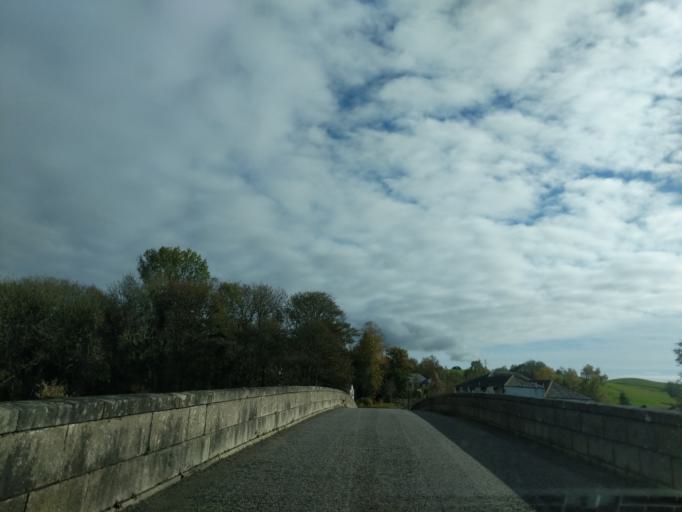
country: GB
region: Scotland
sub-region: Dumfries and Galloway
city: Castle Douglas
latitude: 55.0811
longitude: -4.1316
